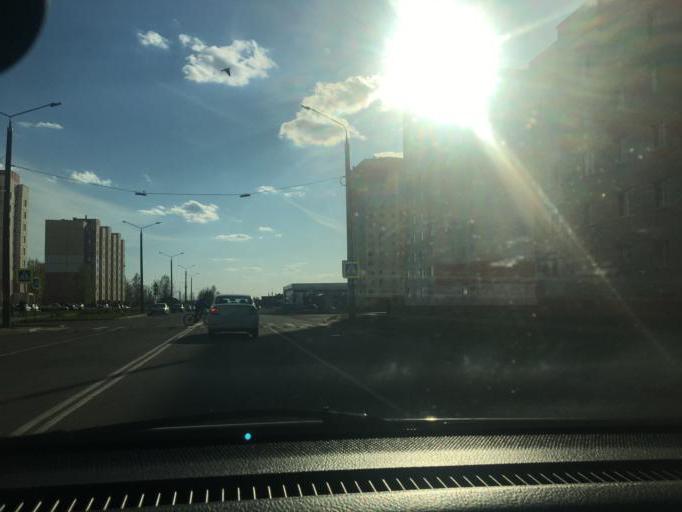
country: BY
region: Mogilev
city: Babruysk
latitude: 53.1621
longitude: 29.1730
